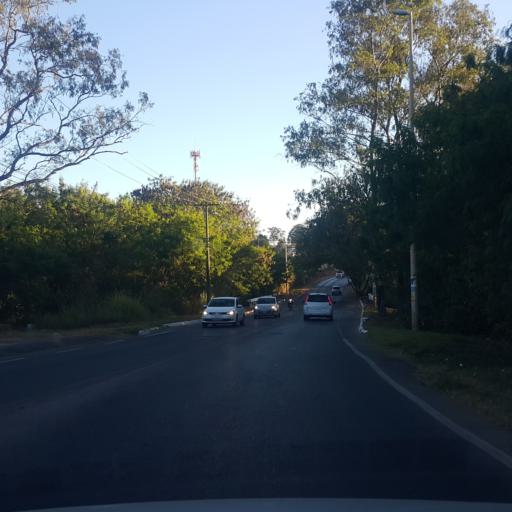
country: BR
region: Federal District
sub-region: Brasilia
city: Brasilia
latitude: -15.8573
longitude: -47.9771
